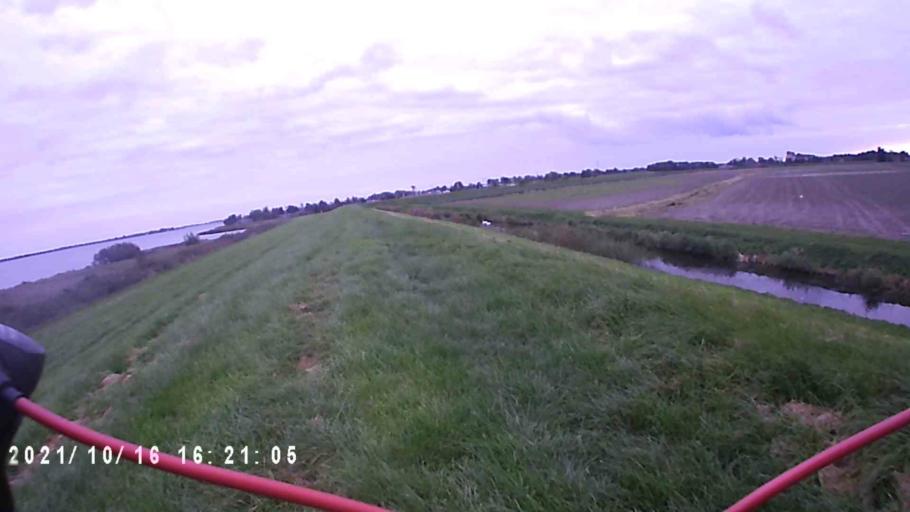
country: NL
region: Friesland
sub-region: Gemeente Dongeradeel
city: Anjum
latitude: 53.3884
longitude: 6.1553
